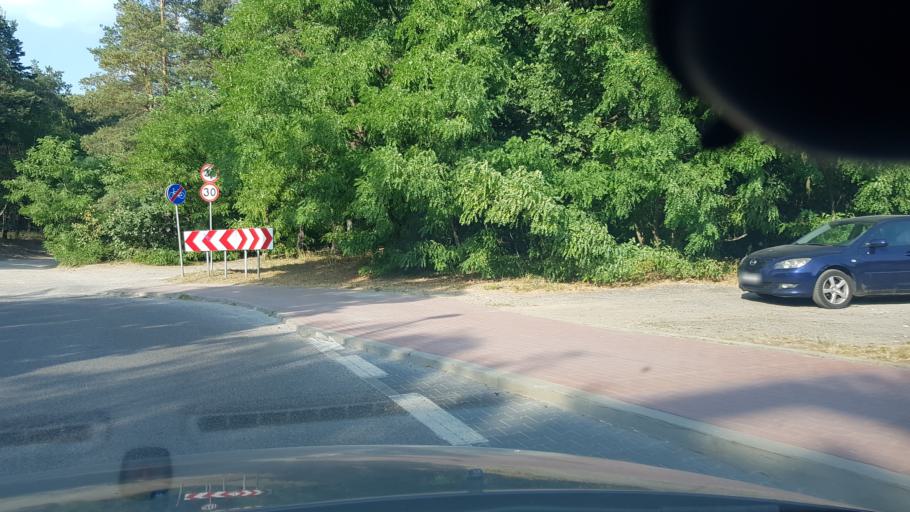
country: PL
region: Masovian Voivodeship
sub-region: Warszawa
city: Bialoleka
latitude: 52.3274
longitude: 20.9576
